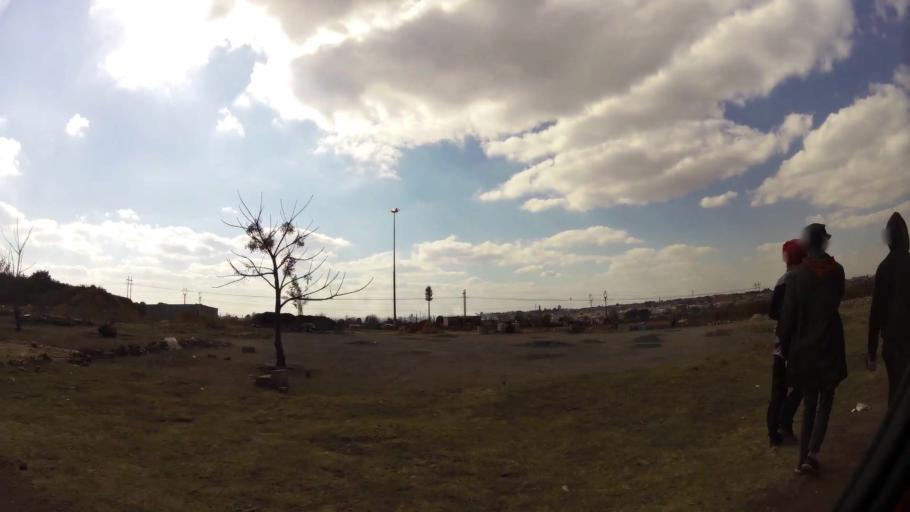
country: ZA
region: Gauteng
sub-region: Ekurhuleni Metropolitan Municipality
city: Tembisa
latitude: -25.9938
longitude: 28.2302
